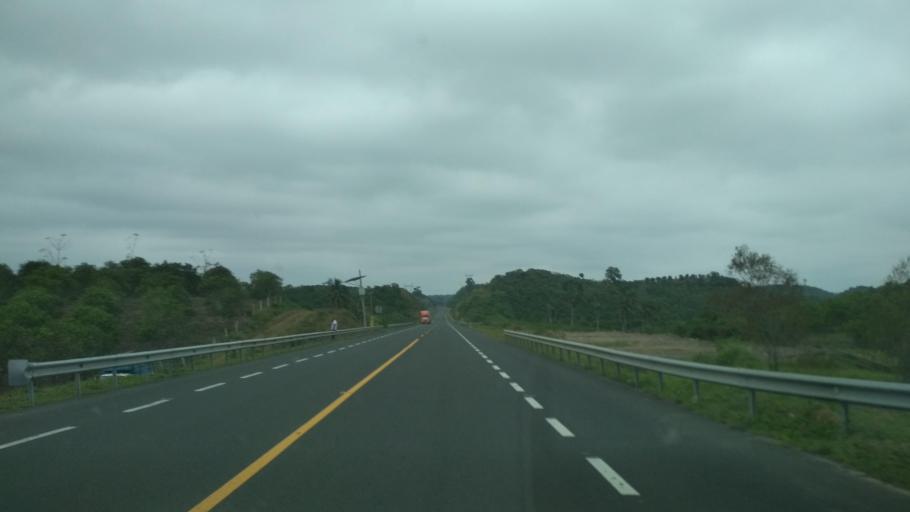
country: MX
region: Veracruz
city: Gutierrez Zamora
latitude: 20.3001
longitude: -97.0850
